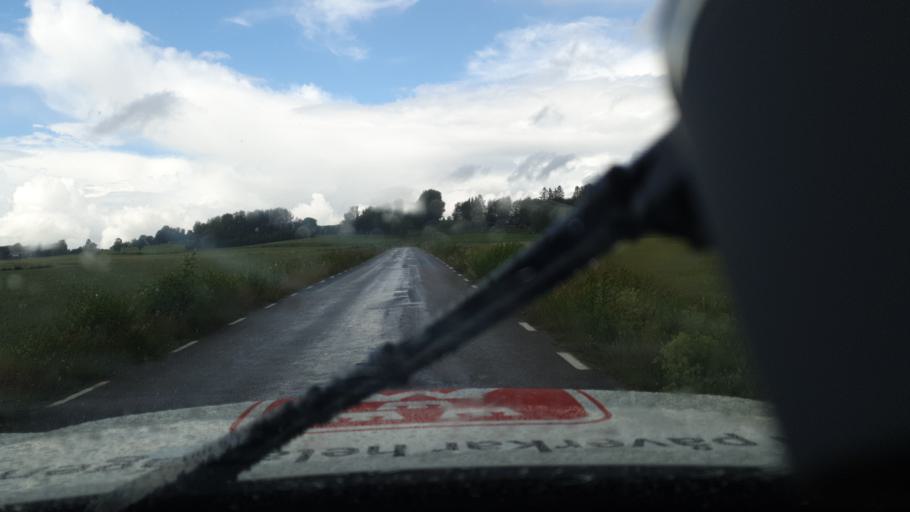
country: SE
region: Vaestra Goetaland
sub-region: Falkopings Kommun
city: Akarp
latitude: 58.1198
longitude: 13.7731
